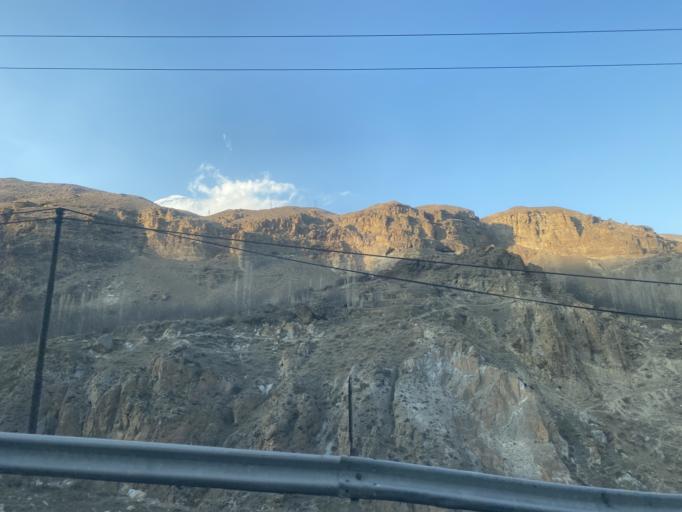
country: IR
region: Tehran
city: Damavand
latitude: 35.8677
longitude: 52.1497
